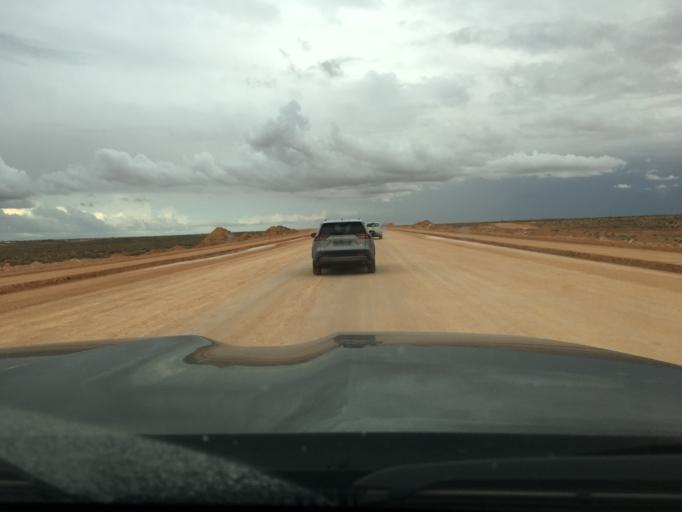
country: TN
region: Madanin
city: Medenine
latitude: 33.2676
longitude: 10.5842
